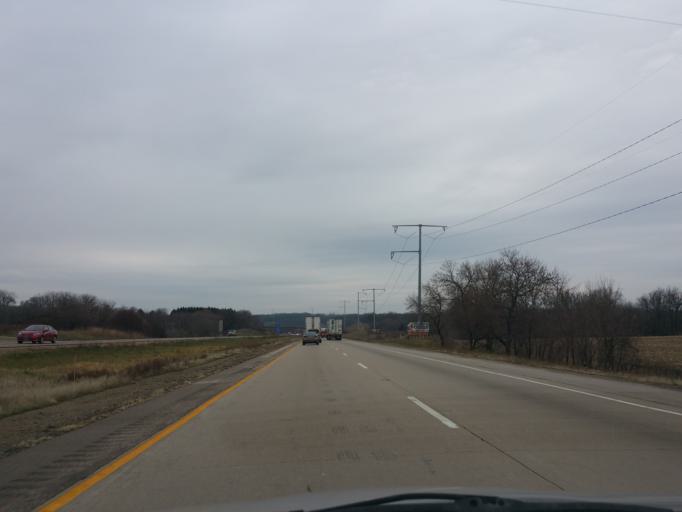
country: US
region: Wisconsin
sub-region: Dane County
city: Deerfield
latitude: 42.9962
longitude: -89.1508
